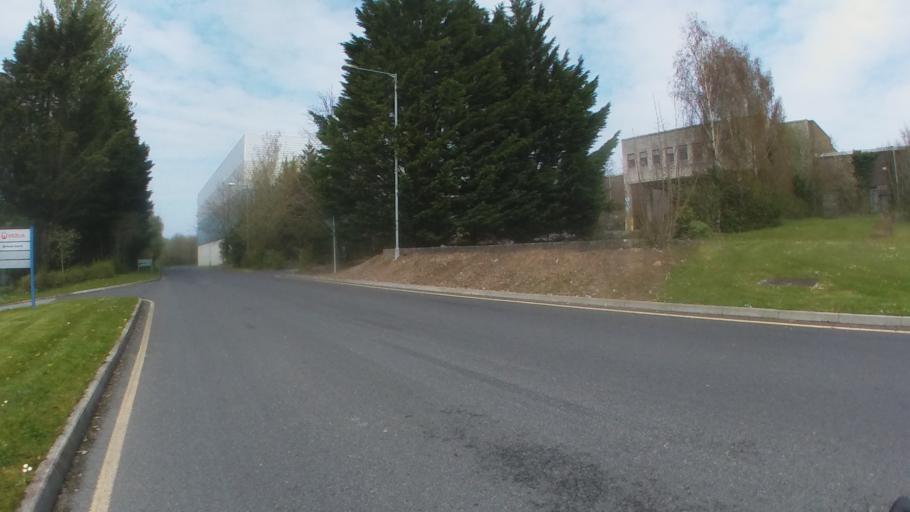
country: IE
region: Leinster
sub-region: Kilkenny
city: Kilkenny
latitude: 52.6439
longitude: -7.2141
